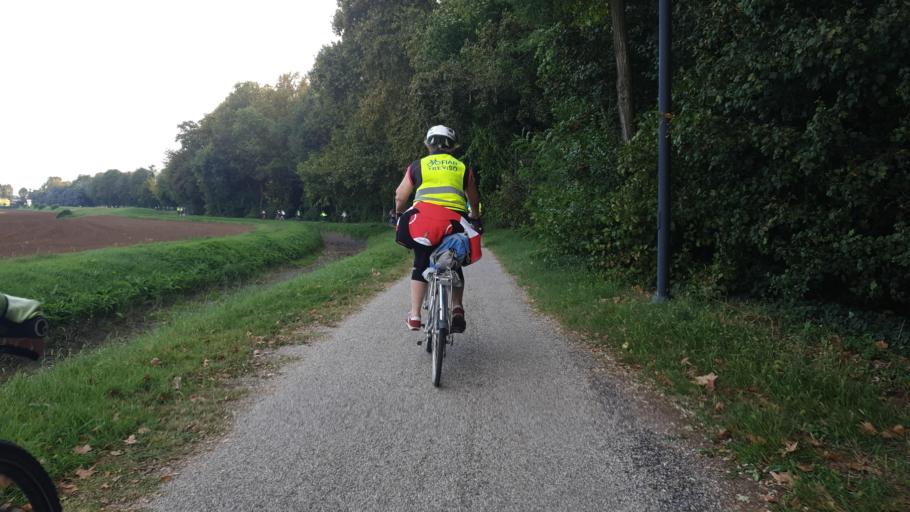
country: IT
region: Veneto
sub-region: Provincia di Padova
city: Montagnana
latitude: 45.2441
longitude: 11.4702
